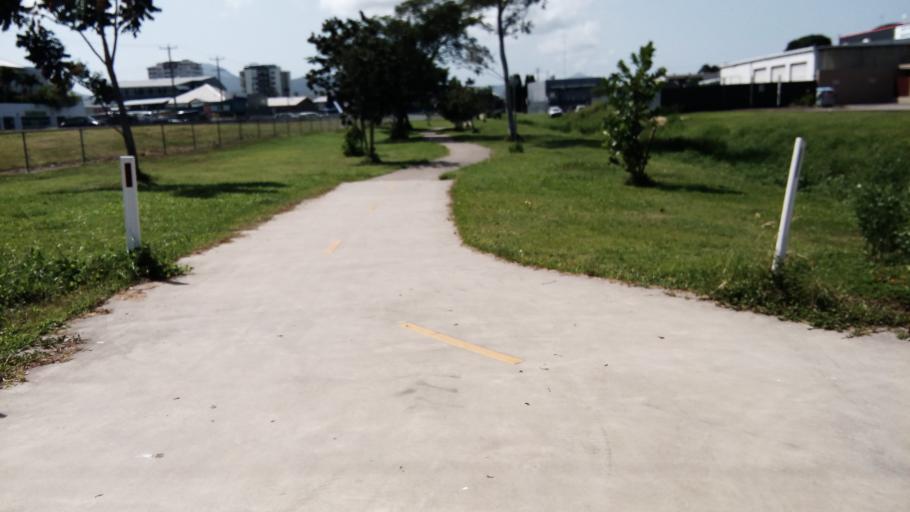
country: AU
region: Queensland
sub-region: Cairns
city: Cairns
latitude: -16.9205
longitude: 145.7671
